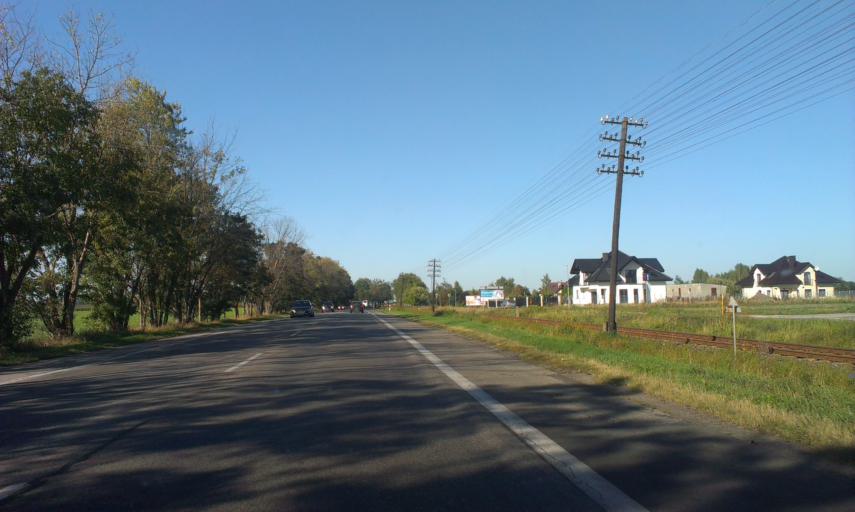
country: PL
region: Kujawsko-Pomorskie
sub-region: Powiat torunski
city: Lysomice
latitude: 53.0765
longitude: 18.6182
